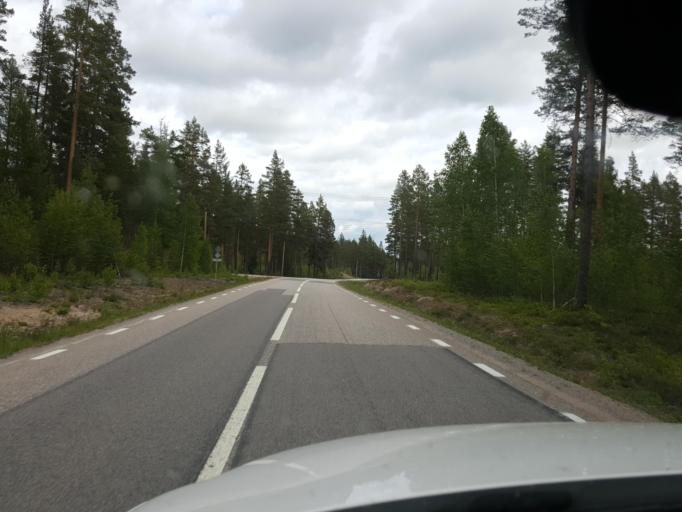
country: SE
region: Gaevleborg
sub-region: Ljusdals Kommun
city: Farila
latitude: 61.7832
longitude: 15.6086
